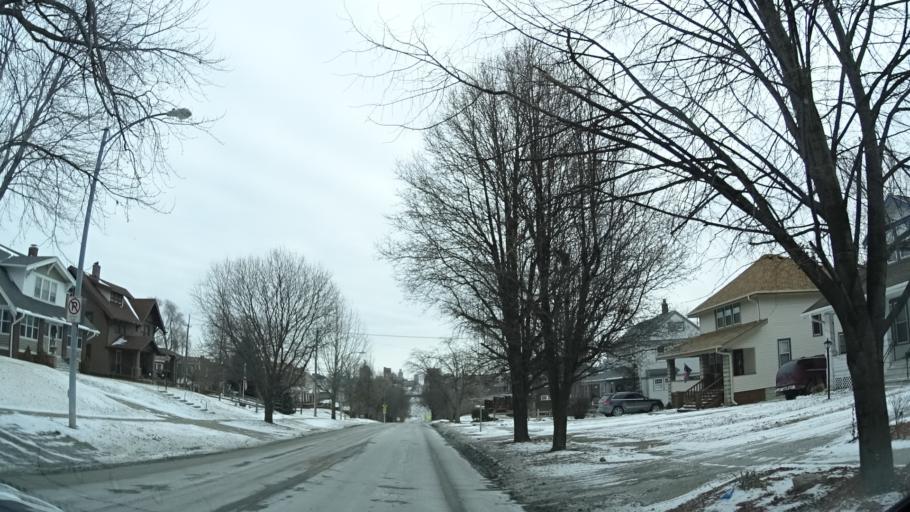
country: US
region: Nebraska
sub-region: Douglas County
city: Omaha
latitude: 41.2578
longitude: -95.9865
